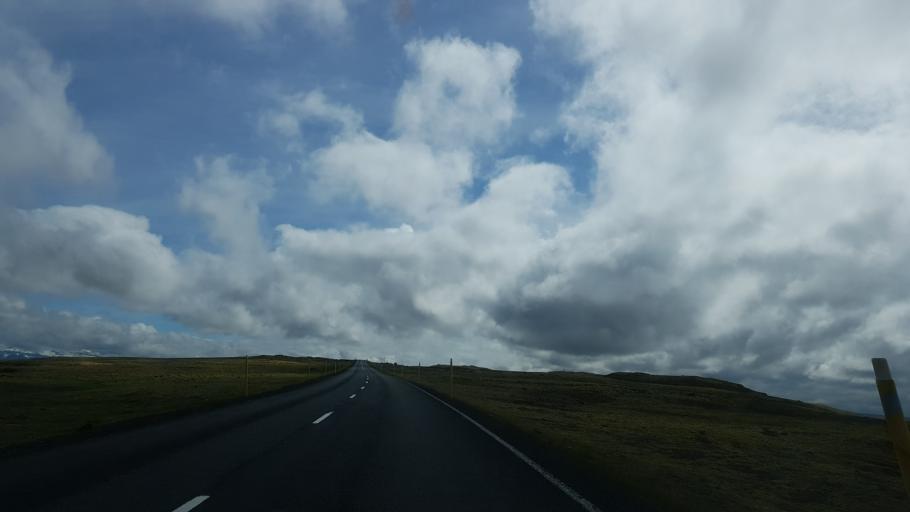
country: IS
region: West
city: Borgarnes
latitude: 64.9972
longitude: -21.0674
